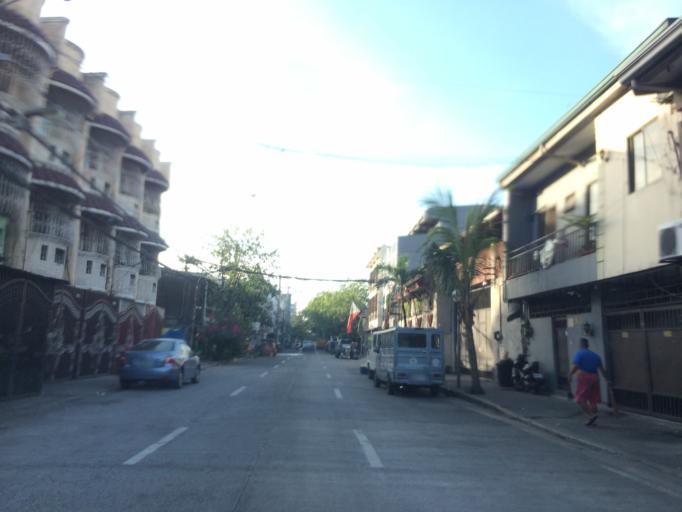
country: PH
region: Metro Manila
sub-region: City of Manila
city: Manila
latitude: 14.6169
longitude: 120.9901
